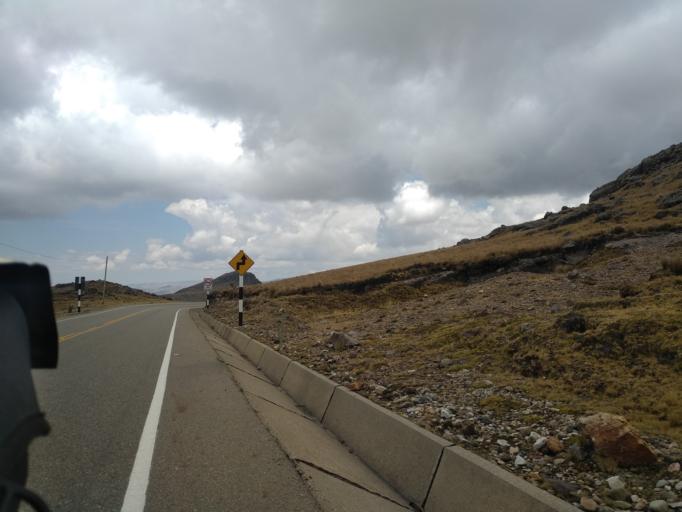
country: PE
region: La Libertad
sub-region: Provincia de Santiago de Chuco
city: Quiruvilca
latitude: -7.9697
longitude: -78.2049
